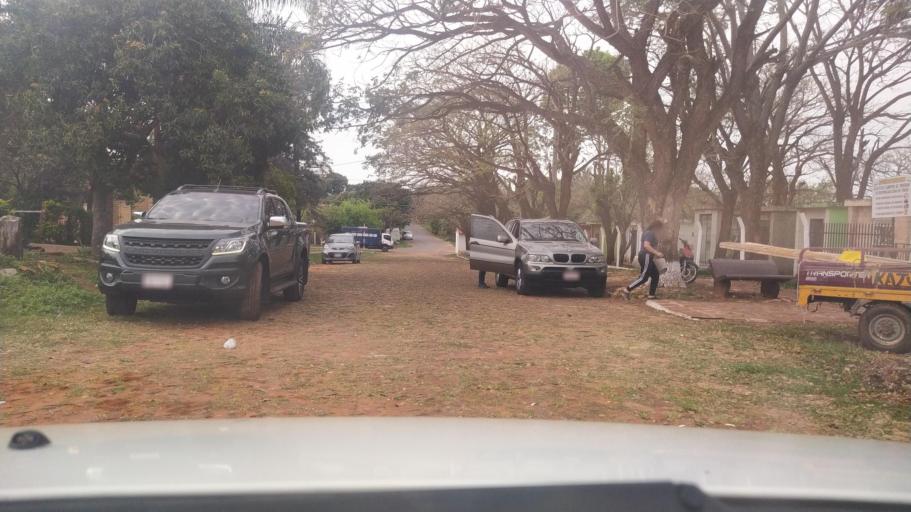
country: PY
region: Misiones
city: San Juan Bautista
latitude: -26.6699
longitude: -57.1537
